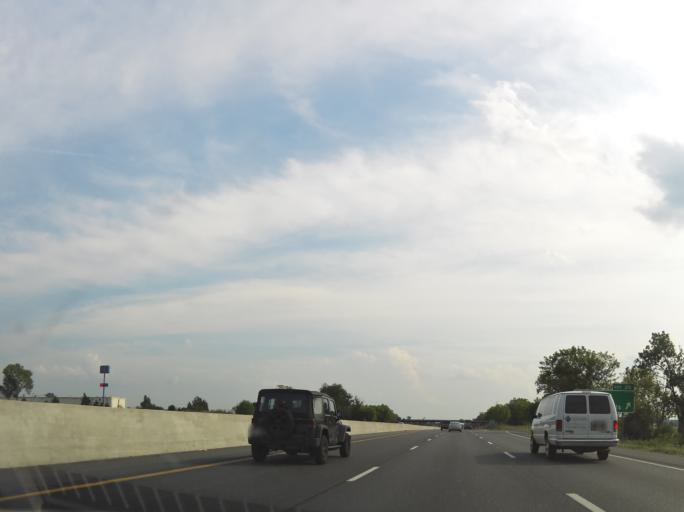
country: US
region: Maryland
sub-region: Washington County
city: Williamsport
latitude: 39.5496
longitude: -77.9096
